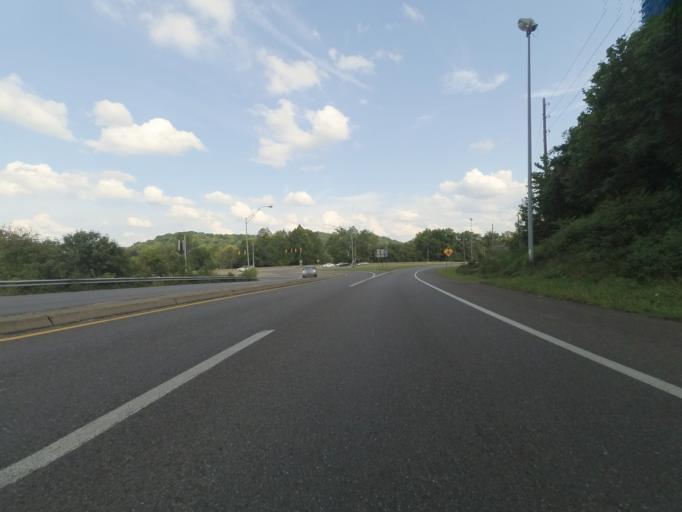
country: US
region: West Virginia
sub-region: Cabell County
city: Huntington
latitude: 38.4223
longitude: -82.3932
